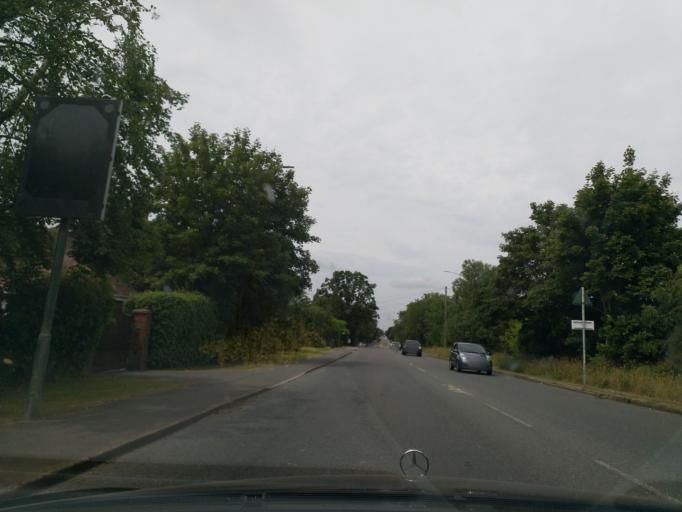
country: GB
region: England
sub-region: Solihull
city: Balsall Common
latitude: 52.3849
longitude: -1.6454
